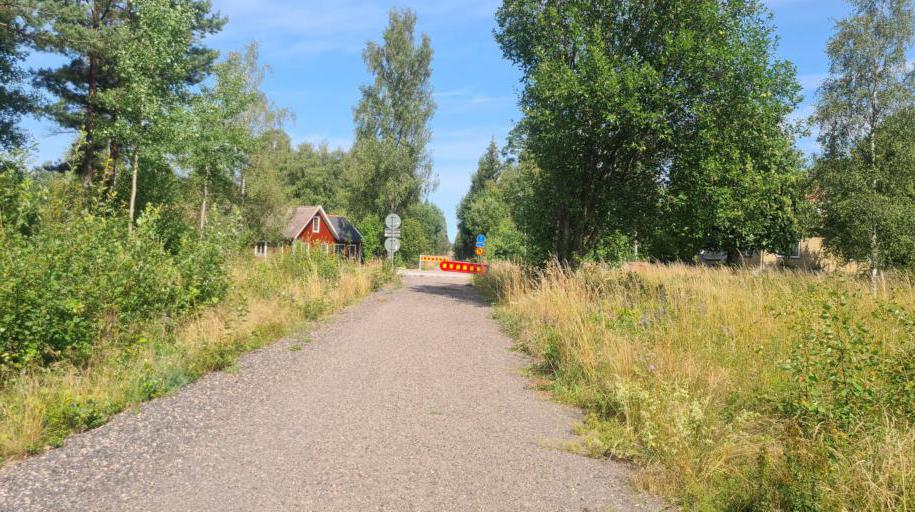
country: SE
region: Kronoberg
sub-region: Ljungby Kommun
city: Lagan
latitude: 56.9720
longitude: 13.9502
